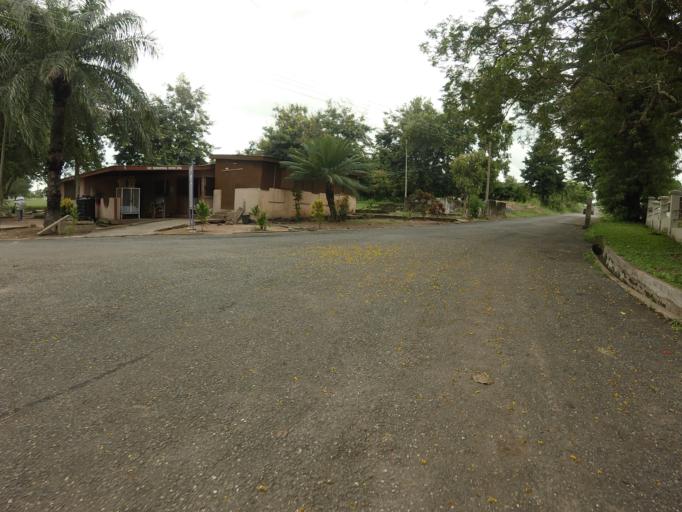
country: GH
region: Volta
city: Ho
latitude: 6.5899
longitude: 0.4671
